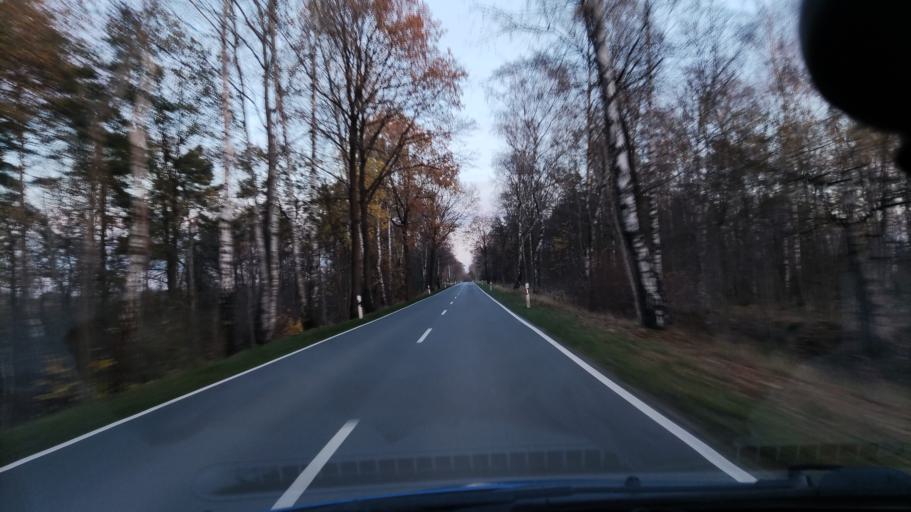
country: DE
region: Lower Saxony
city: Schneverdingen
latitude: 53.1256
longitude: 9.8247
